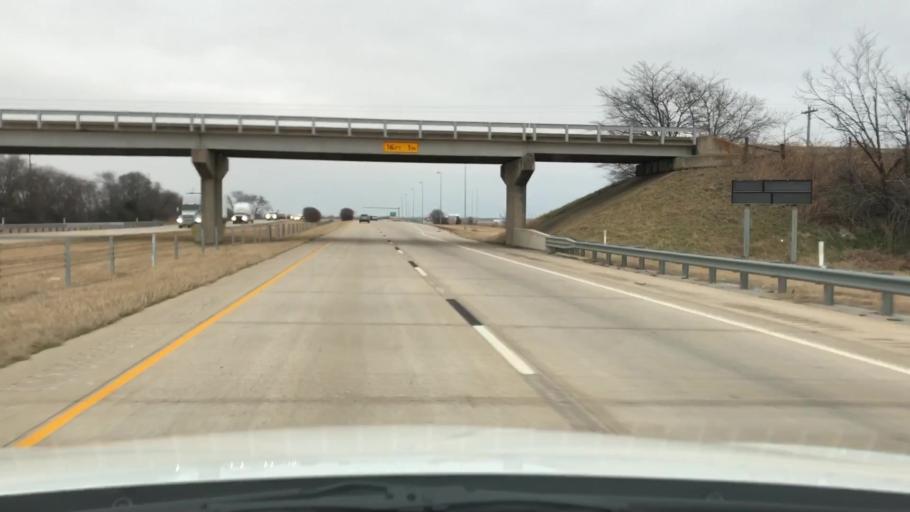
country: US
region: Oklahoma
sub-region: Love County
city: Marietta
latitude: 33.8966
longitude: -97.1343
